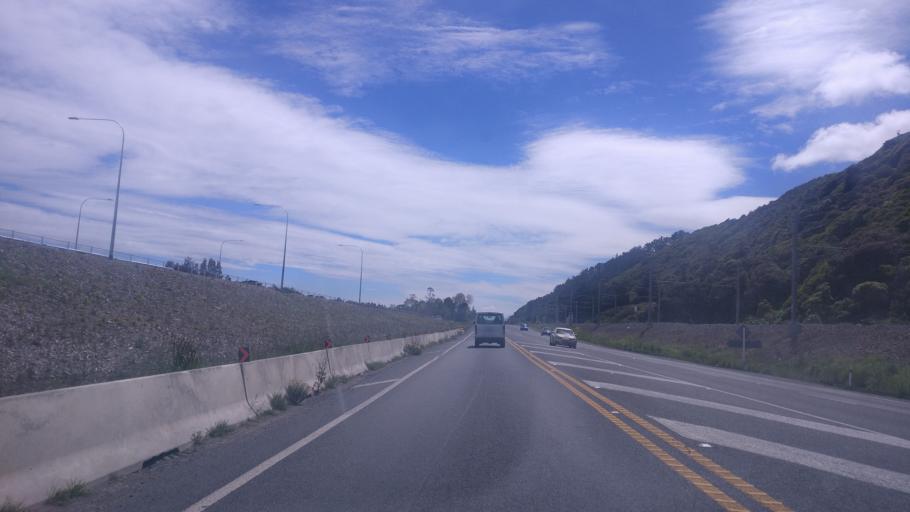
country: NZ
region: Wellington
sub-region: Kapiti Coast District
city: Paraparaumu
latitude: -40.9390
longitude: 174.9938
